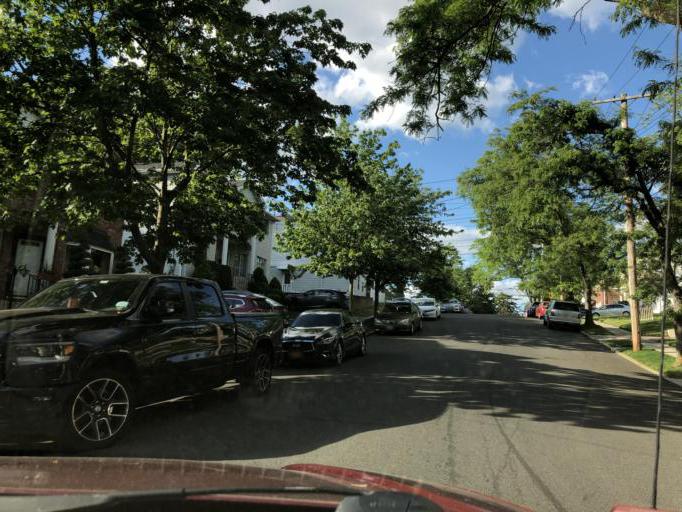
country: US
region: New York
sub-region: Richmond County
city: Staten Island
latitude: 40.5956
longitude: -74.0920
